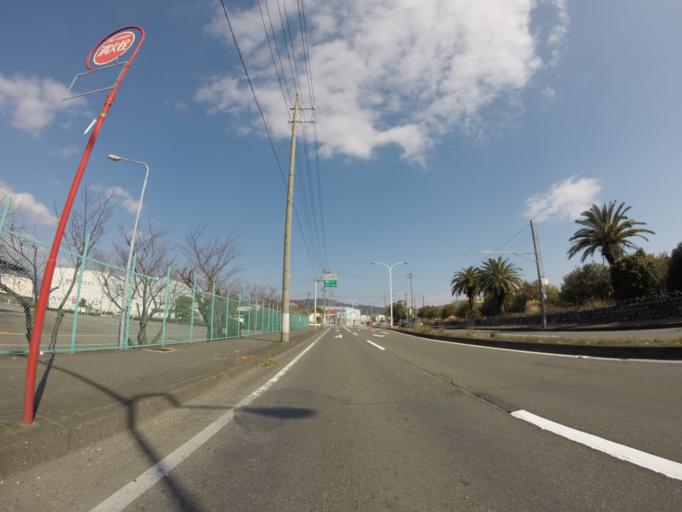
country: JP
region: Shizuoka
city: Shizuoka-shi
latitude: 35.0289
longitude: 138.4921
